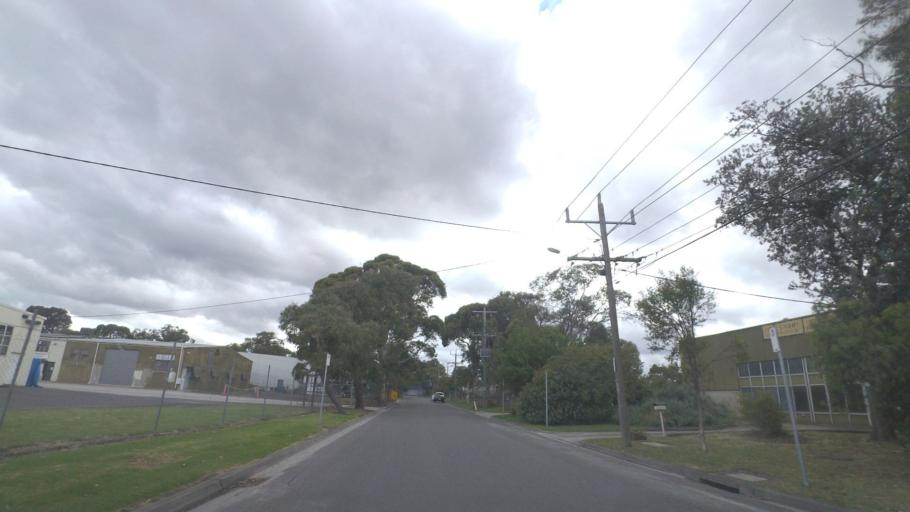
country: AU
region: Victoria
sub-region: Maroondah
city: Croydon South
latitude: -37.8239
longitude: 145.2802
